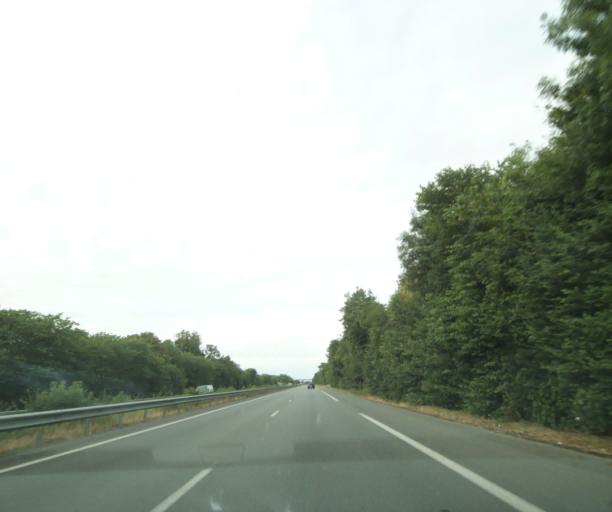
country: FR
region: Poitou-Charentes
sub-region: Departement de la Charente-Maritime
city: Dompierre-sur-Mer
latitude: 46.1864
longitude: -1.0762
